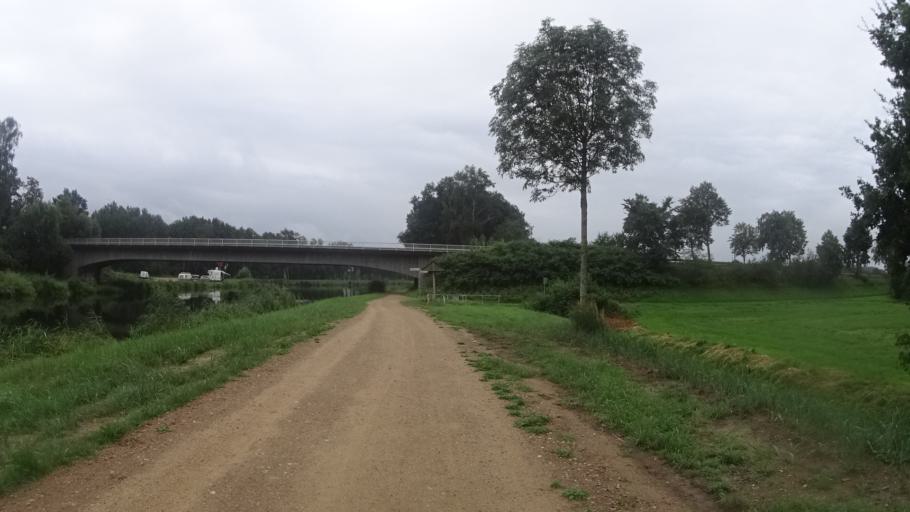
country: DE
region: Schleswig-Holstein
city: Buchen
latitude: 53.4802
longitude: 10.6310
